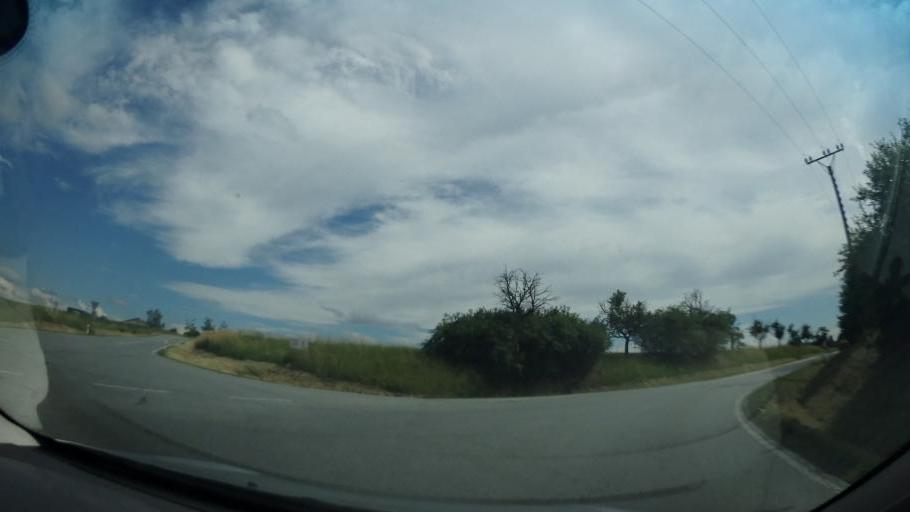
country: CZ
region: South Moravian
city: Zastavka
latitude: 49.1741
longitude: 16.3618
